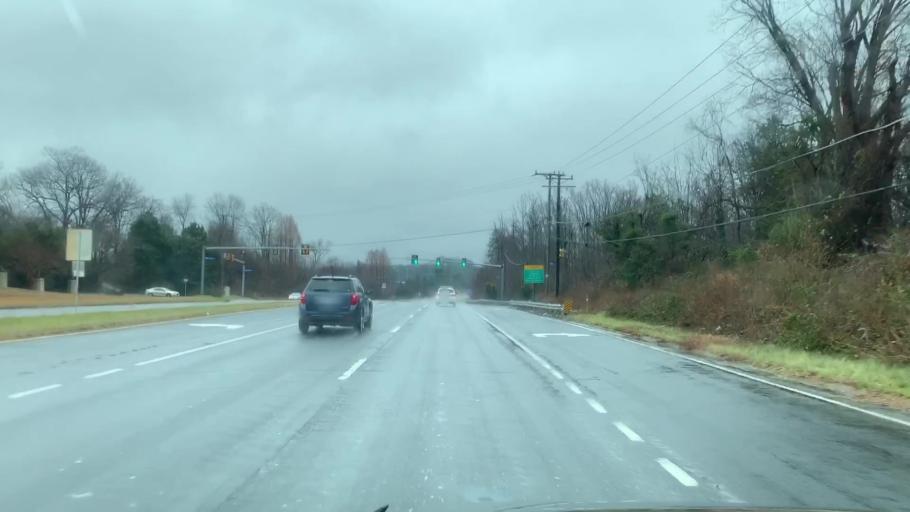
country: US
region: Virginia
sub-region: Fairfax County
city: Fairfax Station
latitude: 38.7674
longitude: -77.3147
